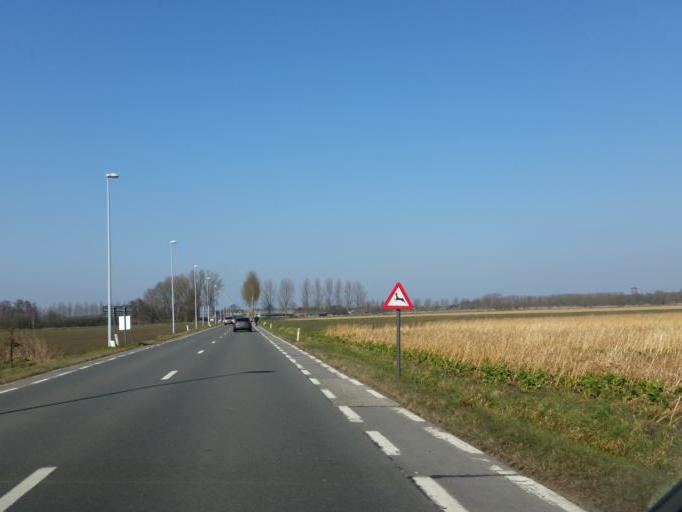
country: BE
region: Flanders
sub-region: Provincie Oost-Vlaanderen
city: Wachtebeke
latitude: 51.1538
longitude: 3.8635
